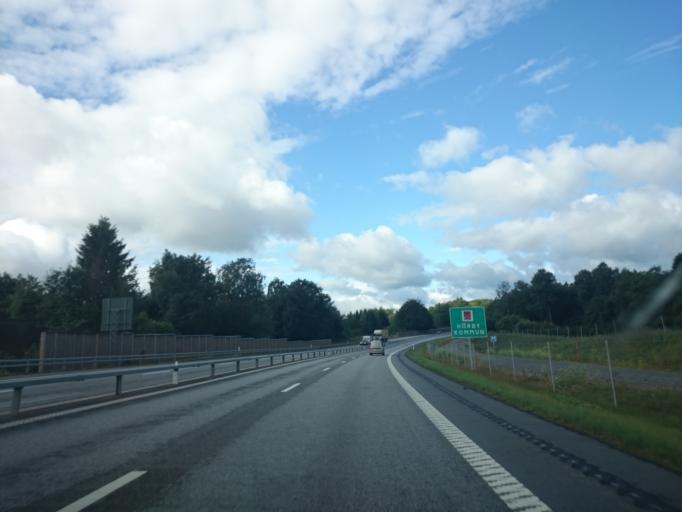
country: SE
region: Skane
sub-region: Horby Kommun
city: Hoerby
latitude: 55.9134
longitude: 13.7711
